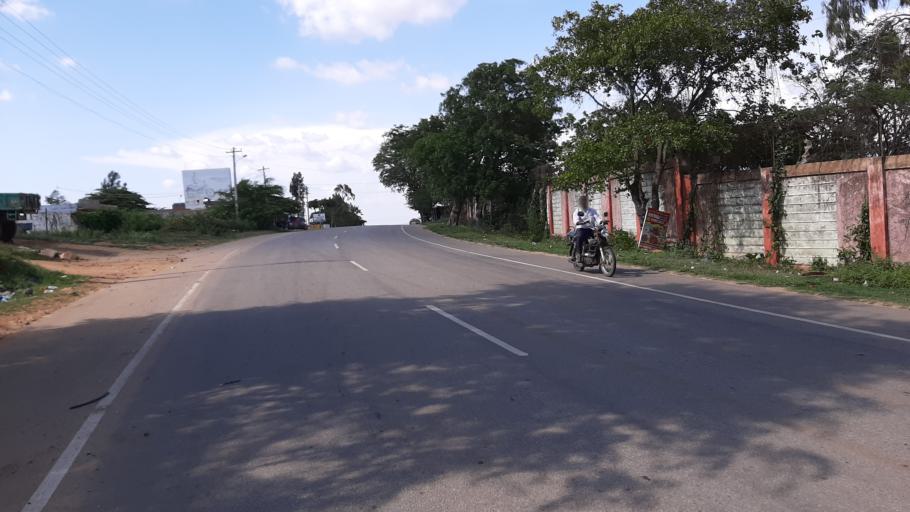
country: IN
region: Tamil Nadu
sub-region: Krishnagiri
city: Denkanikota
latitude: 12.5379
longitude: 77.7888
